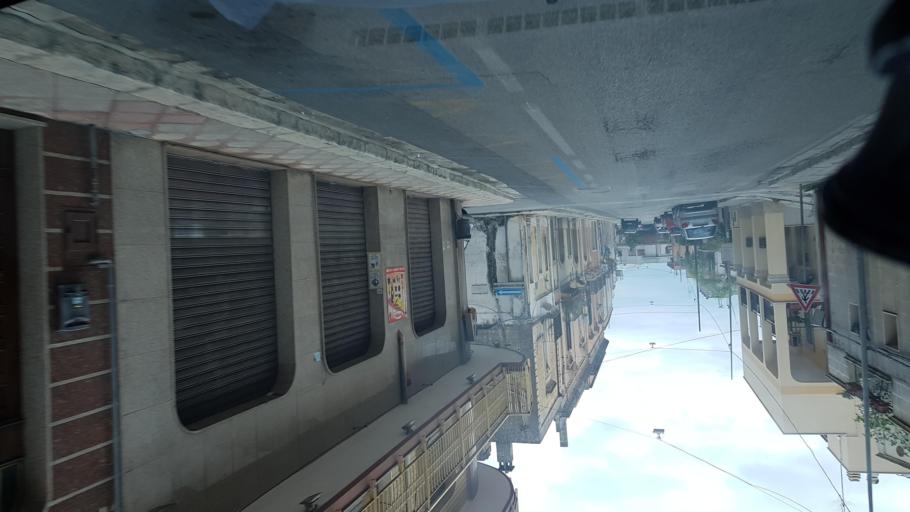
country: IT
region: Apulia
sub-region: Provincia di Brindisi
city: Oria
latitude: 40.5009
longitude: 17.6428
